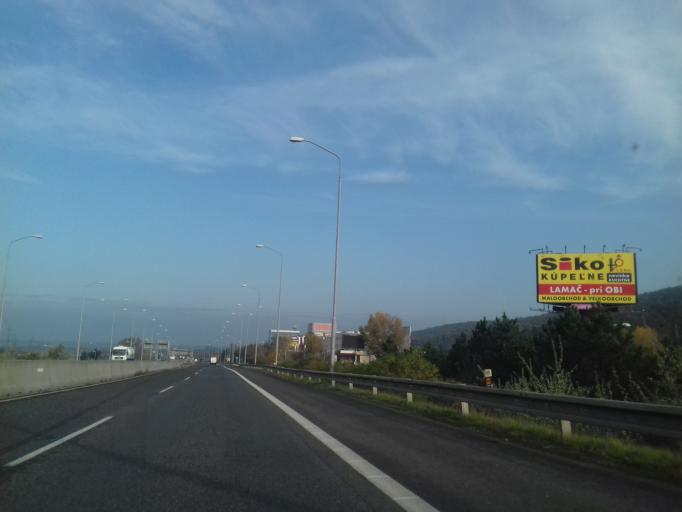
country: SK
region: Bratislavsky
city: Stupava
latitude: 48.2030
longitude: 17.0409
